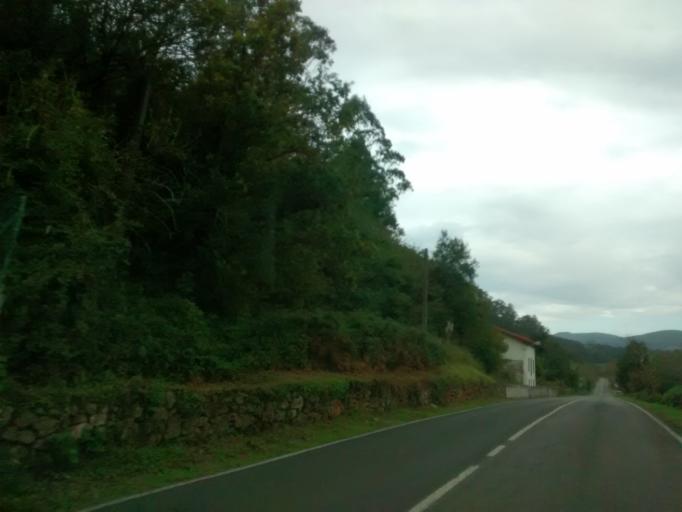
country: ES
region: Cantabria
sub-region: Provincia de Cantabria
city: Entrambasaguas
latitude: 43.3449
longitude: -3.6848
